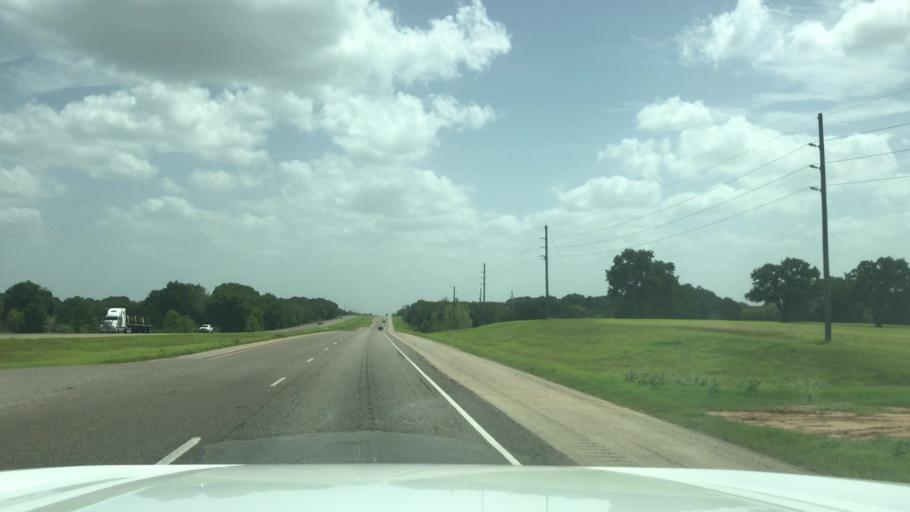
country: US
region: Texas
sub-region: Robertson County
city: Calvert
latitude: 31.0920
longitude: -96.7147
